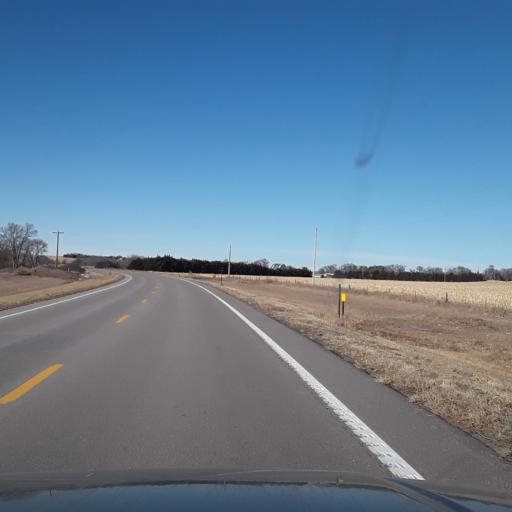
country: US
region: Nebraska
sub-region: Dawson County
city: Cozad
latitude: 40.6885
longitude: -100.1398
